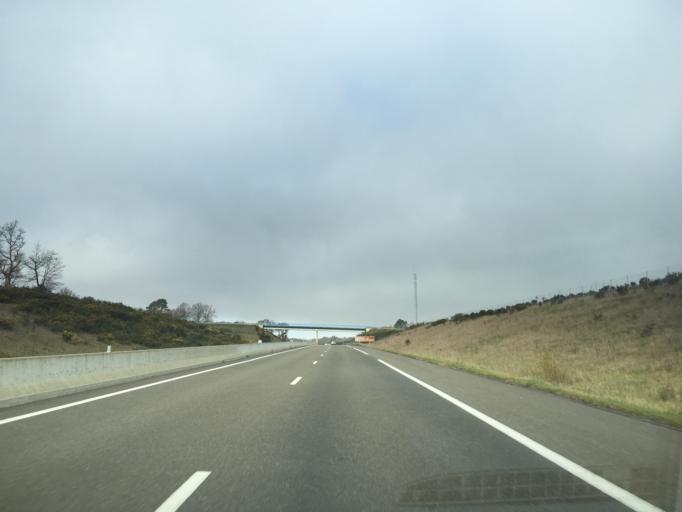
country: FR
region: Aquitaine
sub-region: Departement des Landes
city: Villeneuve-de-Marsan
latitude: 43.8221
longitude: -0.3137
